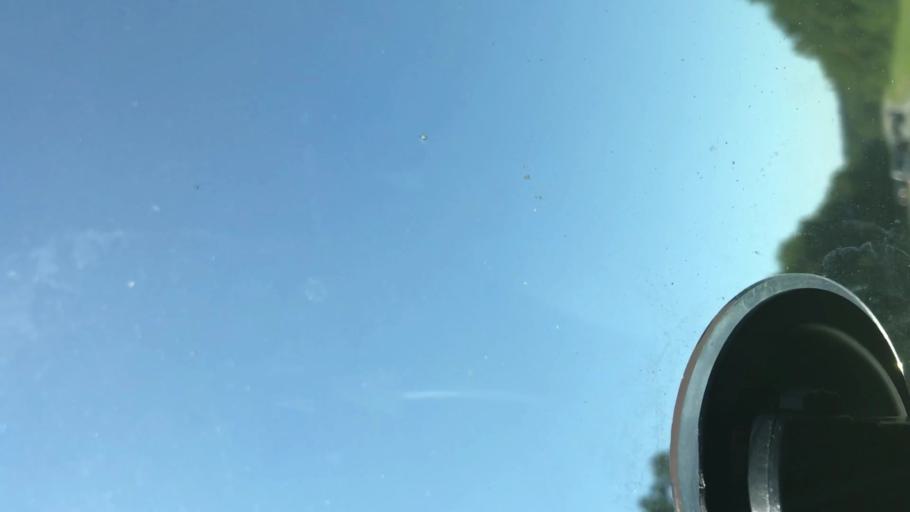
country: US
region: Virginia
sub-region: Spotsylvania County
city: Spotsylvania Courthouse
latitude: 38.1795
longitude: -77.5157
